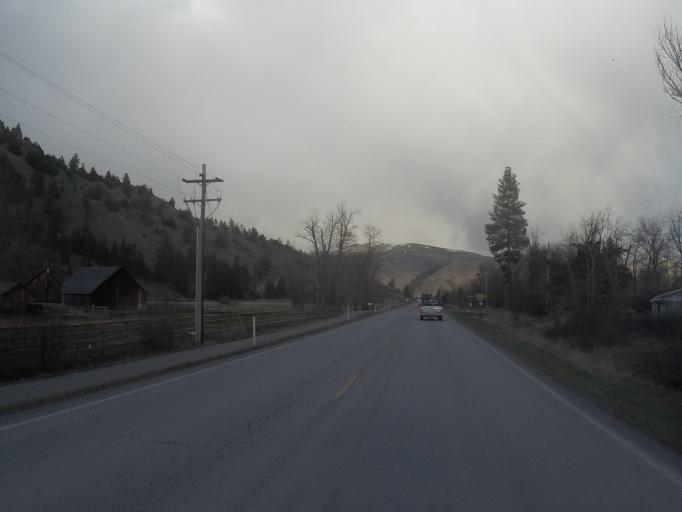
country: US
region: Montana
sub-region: Missoula County
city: Lolo
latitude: 46.7568
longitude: -114.1025
